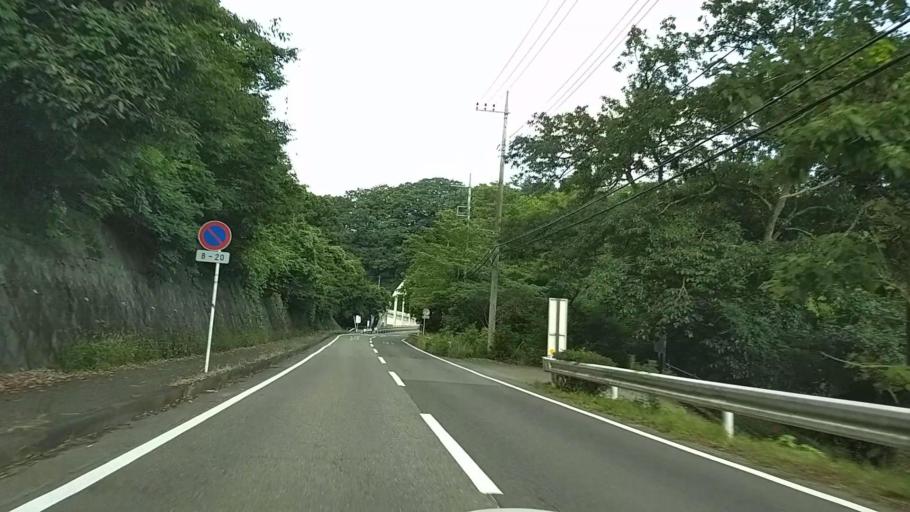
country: JP
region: Yamanashi
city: Uenohara
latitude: 35.6085
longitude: 139.1530
